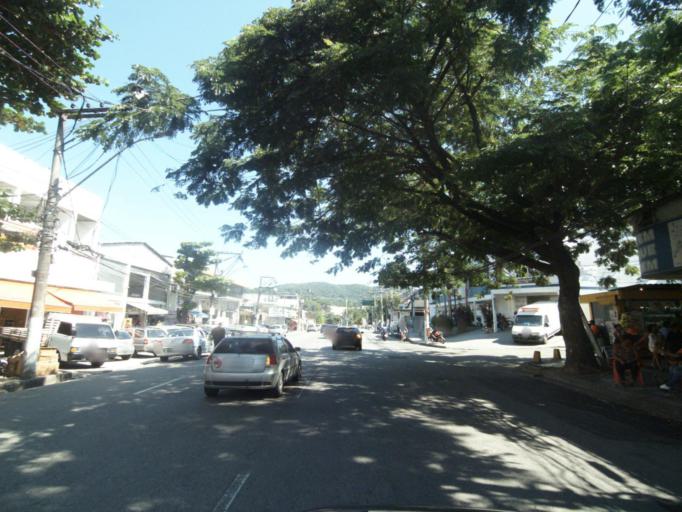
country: BR
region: Rio de Janeiro
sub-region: Niteroi
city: Niteroi
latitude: -22.9072
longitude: -43.0671
